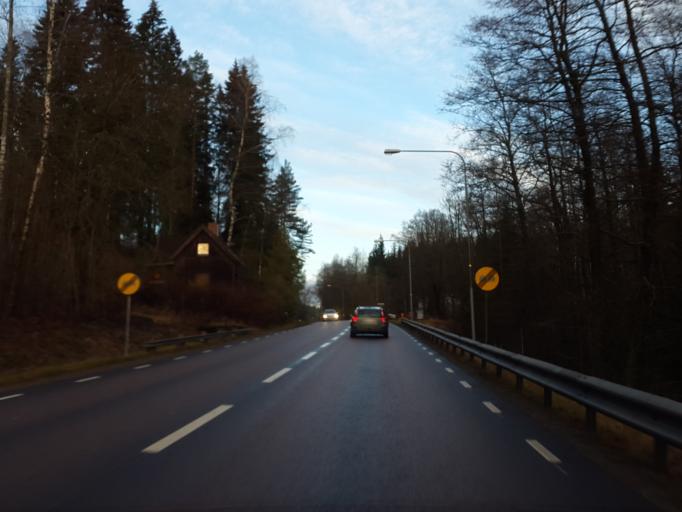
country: SE
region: Vaestra Goetaland
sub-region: Boras Kommun
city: Boras
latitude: 57.7438
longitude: 12.8938
